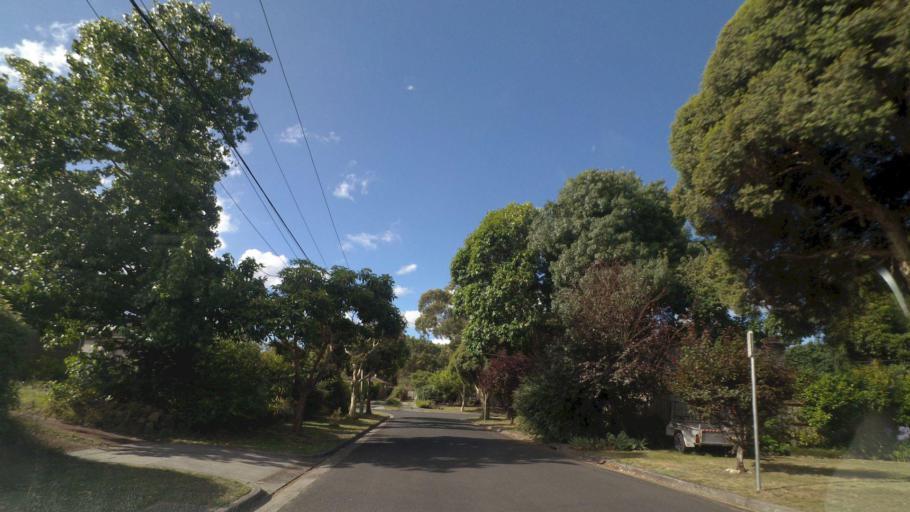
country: AU
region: Victoria
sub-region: Maroondah
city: Warranwood
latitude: -37.7918
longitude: 145.2537
